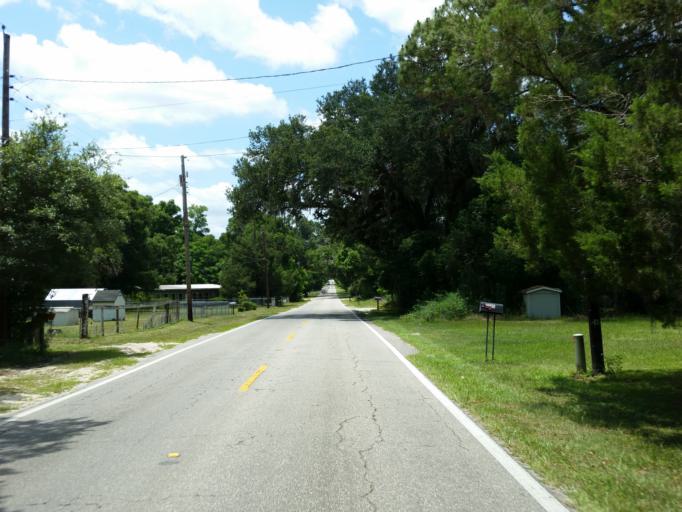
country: US
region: Florida
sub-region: Marion County
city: Belleview
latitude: 29.0113
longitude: -82.0447
